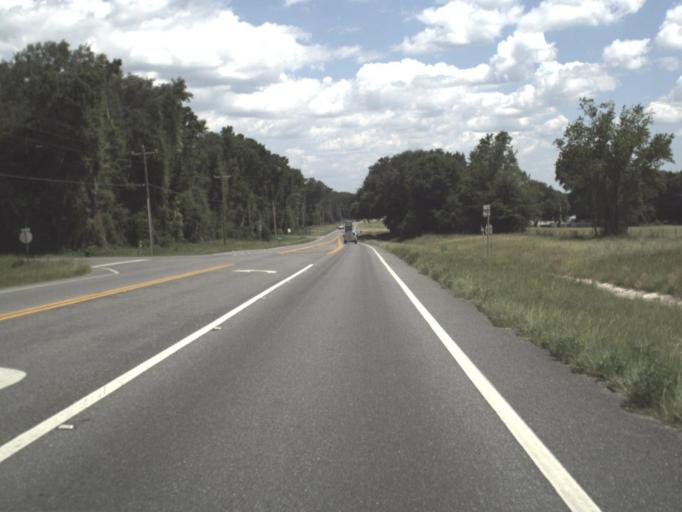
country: US
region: Florida
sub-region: Columbia County
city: Watertown
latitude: 30.1021
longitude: -82.6066
